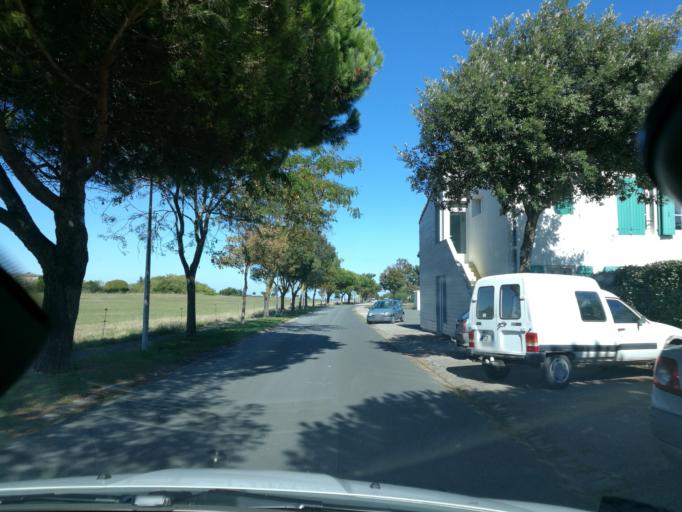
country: FR
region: Poitou-Charentes
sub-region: Departement de la Charente-Maritime
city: Saint-Martin-de-Re
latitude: 46.2011
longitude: -1.3575
